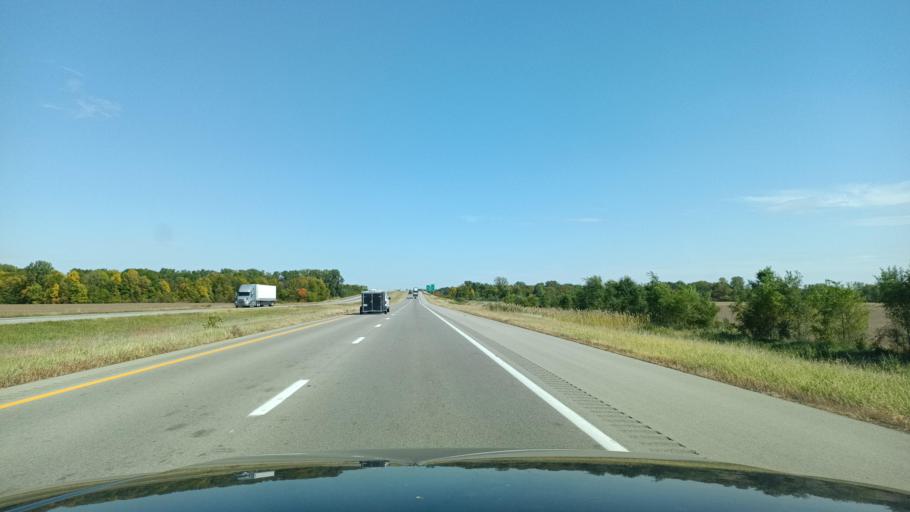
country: US
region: Ohio
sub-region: Henry County
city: Liberty Center
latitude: 41.4165
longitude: -84.0413
